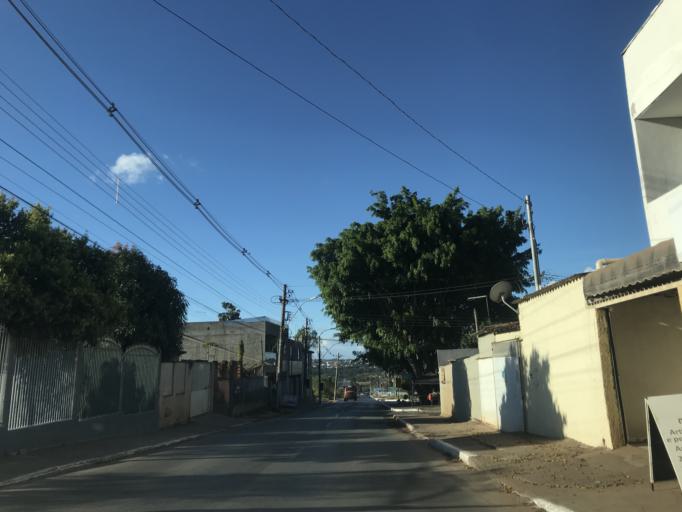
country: BR
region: Federal District
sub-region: Brasilia
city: Brasilia
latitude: -15.8948
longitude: -47.7851
